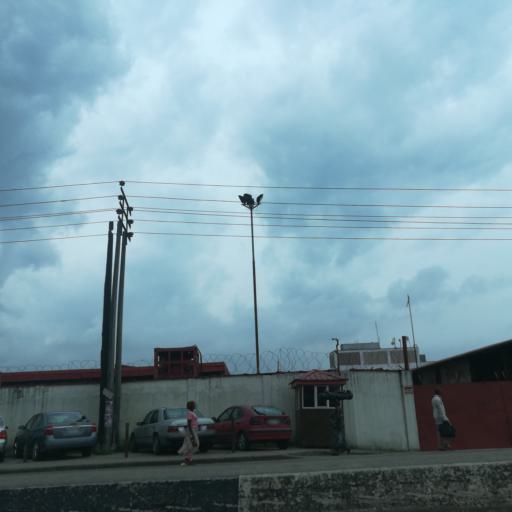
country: NG
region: Rivers
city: Port Harcourt
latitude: 4.8166
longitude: 7.0418
